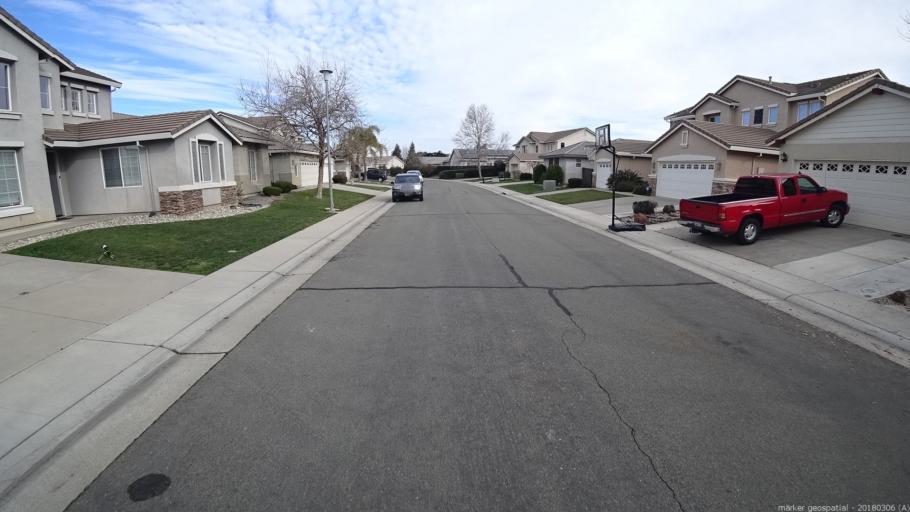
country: US
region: California
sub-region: Sacramento County
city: Vineyard
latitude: 38.4730
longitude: -121.3178
